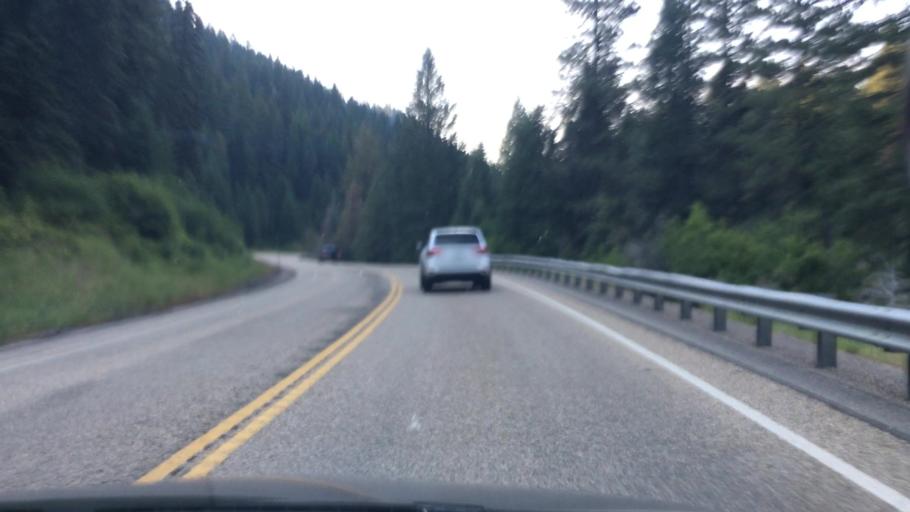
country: US
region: Idaho
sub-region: Valley County
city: Cascade
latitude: 44.1876
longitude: -116.1147
